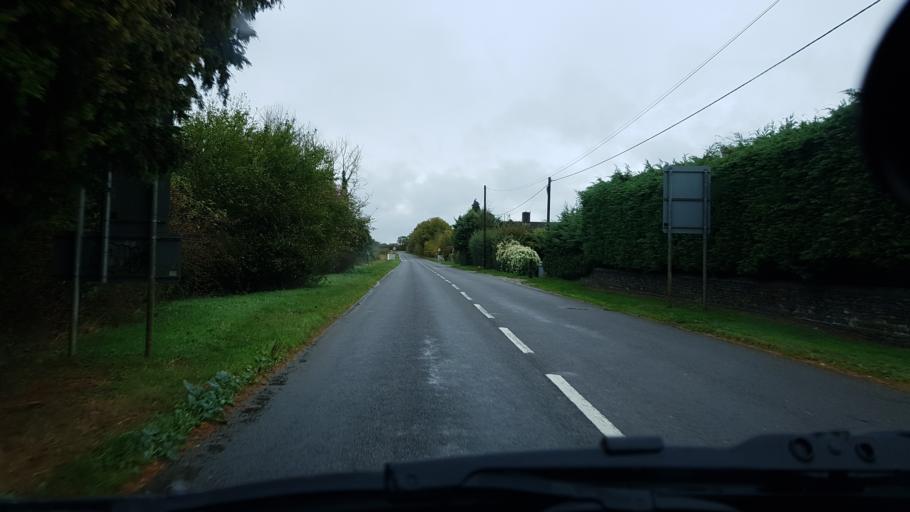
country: GB
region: England
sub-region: Oxfordshire
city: Ducklington
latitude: 51.7305
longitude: -1.4450
